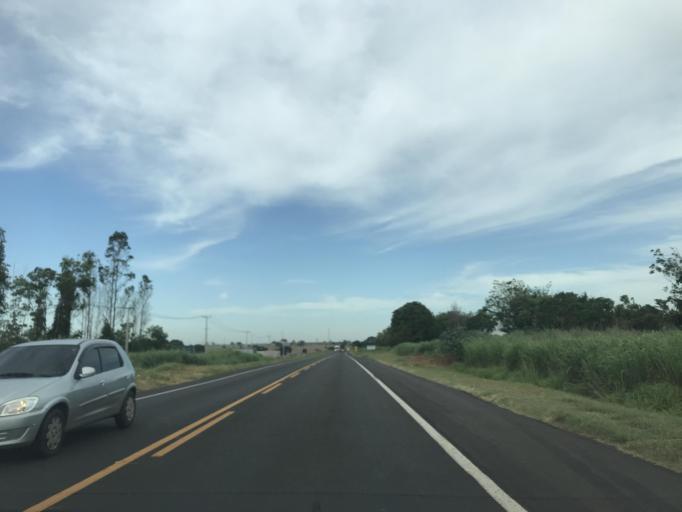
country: BR
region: Parana
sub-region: Paranavai
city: Paranavai
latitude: -23.0142
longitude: -52.5189
